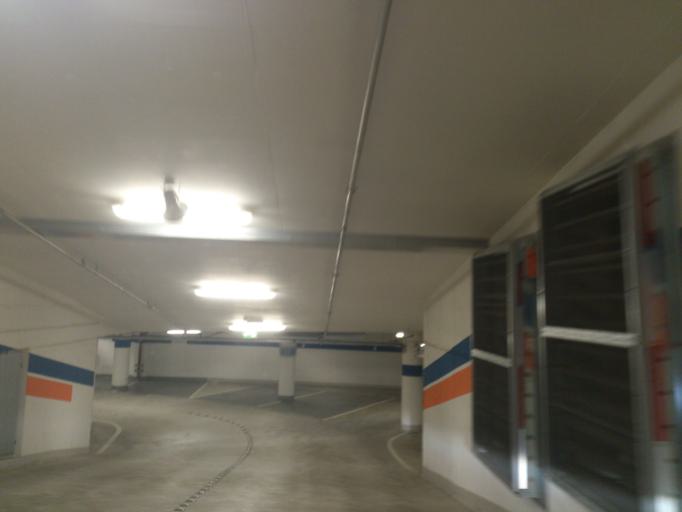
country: DE
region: North Rhine-Westphalia
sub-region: Regierungsbezirk Detmold
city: Paderborn
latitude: 51.7178
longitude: 8.7566
